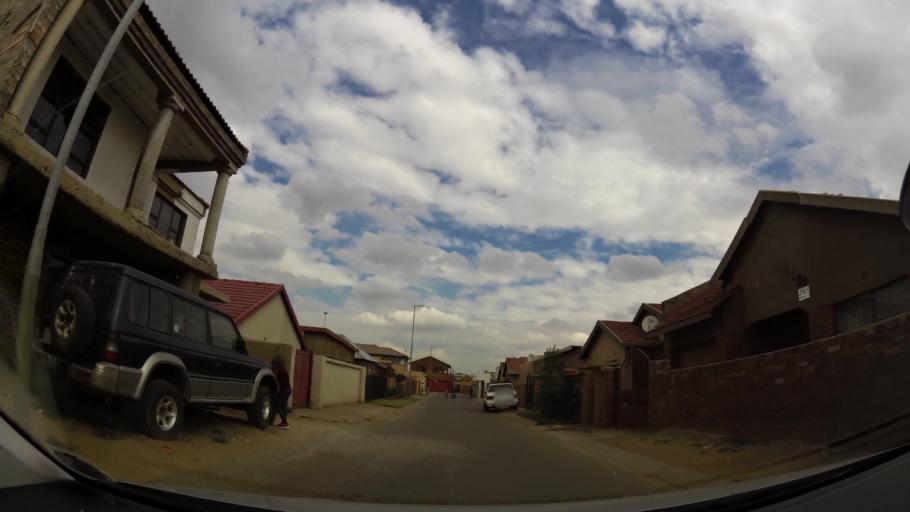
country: ZA
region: Gauteng
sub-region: City of Johannesburg Metropolitan Municipality
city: Soweto
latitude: -26.2732
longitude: 27.8555
